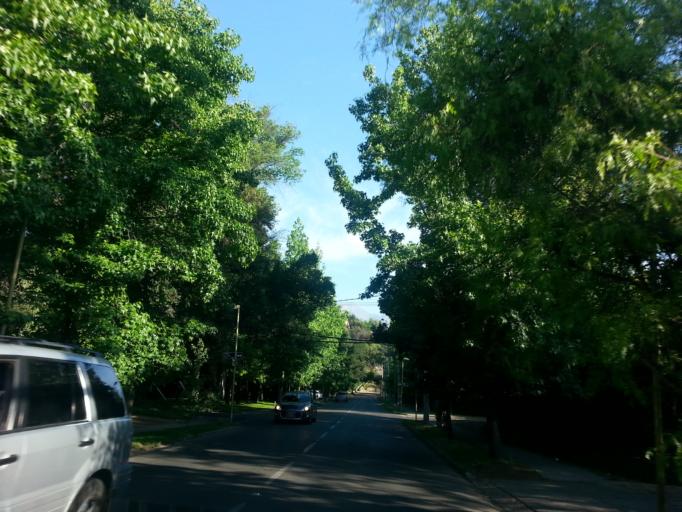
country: CL
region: Santiago Metropolitan
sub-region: Provincia de Santiago
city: Villa Presidente Frei, Nunoa, Santiago, Chile
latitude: -33.3833
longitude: -70.5206
